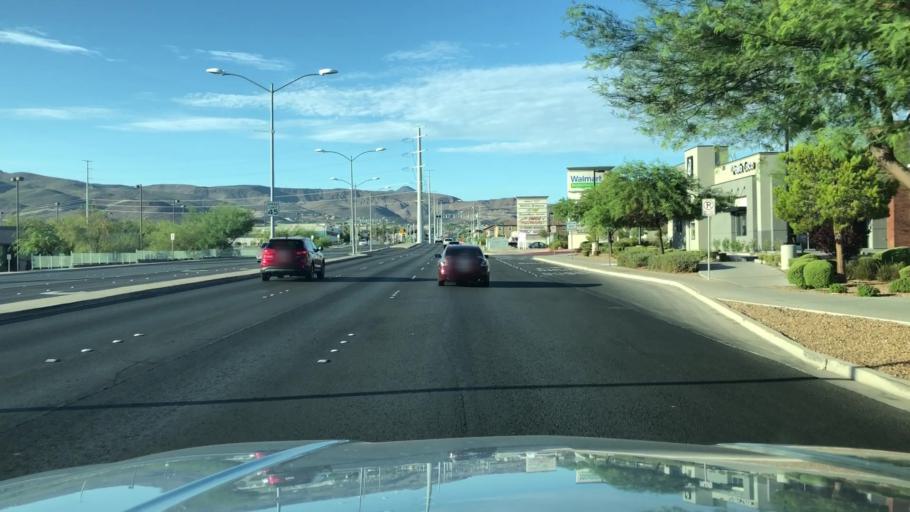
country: US
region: Nevada
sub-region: Clark County
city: Whitney
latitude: 36.0412
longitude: -115.0469
